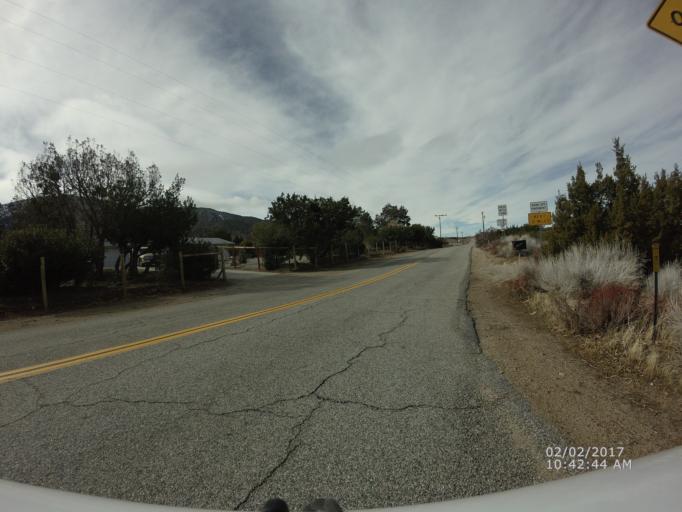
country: US
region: California
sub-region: Los Angeles County
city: Littlerock
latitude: 34.4464
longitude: -117.9361
